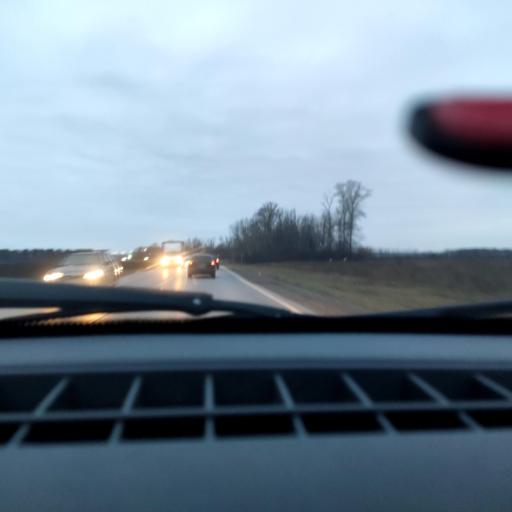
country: RU
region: Bashkortostan
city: Avdon
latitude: 54.5991
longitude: 55.8246
